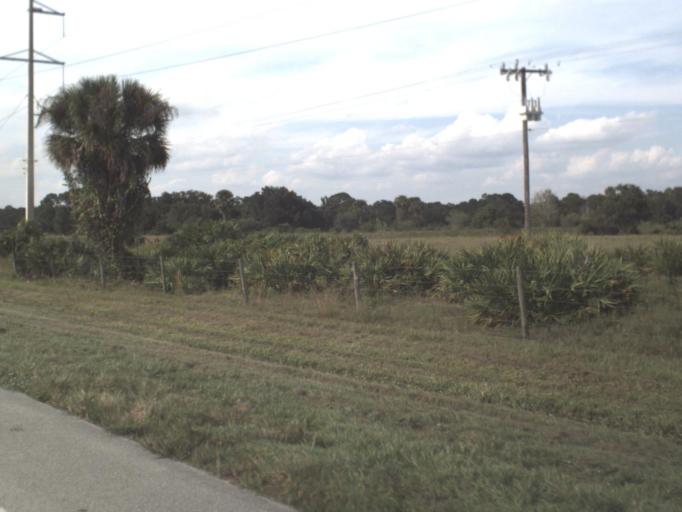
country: US
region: Florida
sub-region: Okeechobee County
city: Taylor Creek
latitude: 27.1707
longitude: -80.6949
